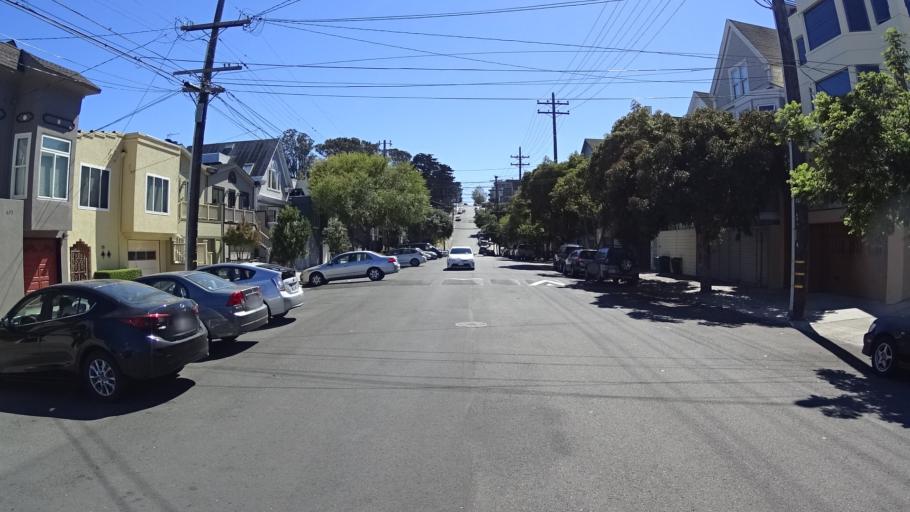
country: US
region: California
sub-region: San Francisco County
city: San Francisco
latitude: 37.7583
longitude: -122.3981
